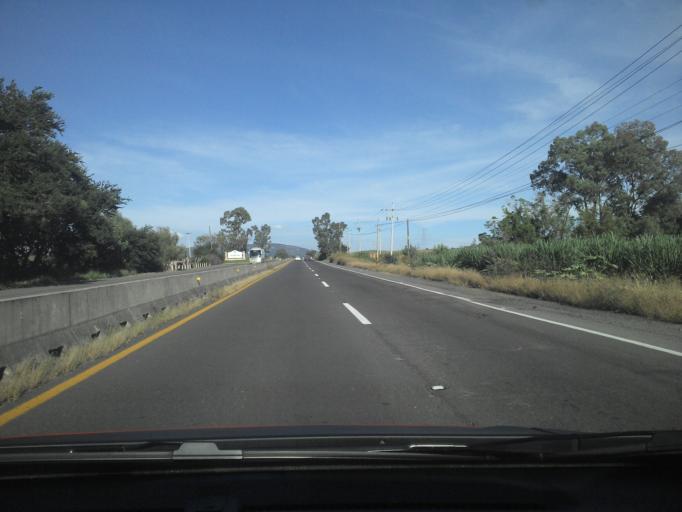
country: MX
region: Jalisco
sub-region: Tala
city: Los Ruisenores
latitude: 20.7081
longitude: -103.6735
